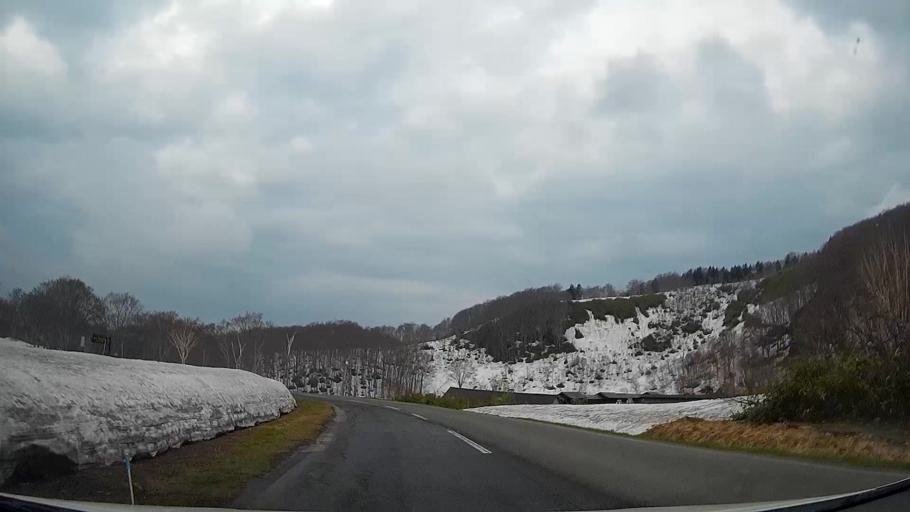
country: JP
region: Aomori
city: Aomori Shi
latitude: 40.6495
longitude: 140.8512
